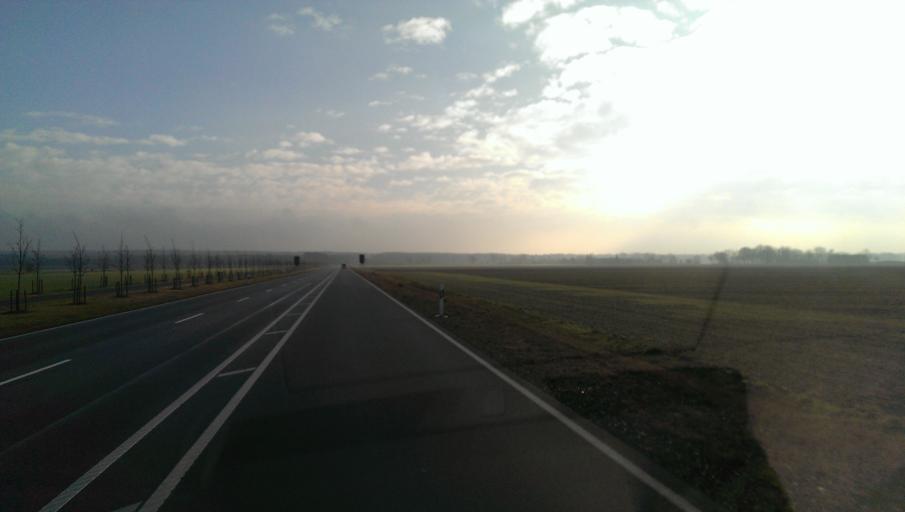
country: DE
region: Brandenburg
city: Herzberg
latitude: 51.6678
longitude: 13.2737
